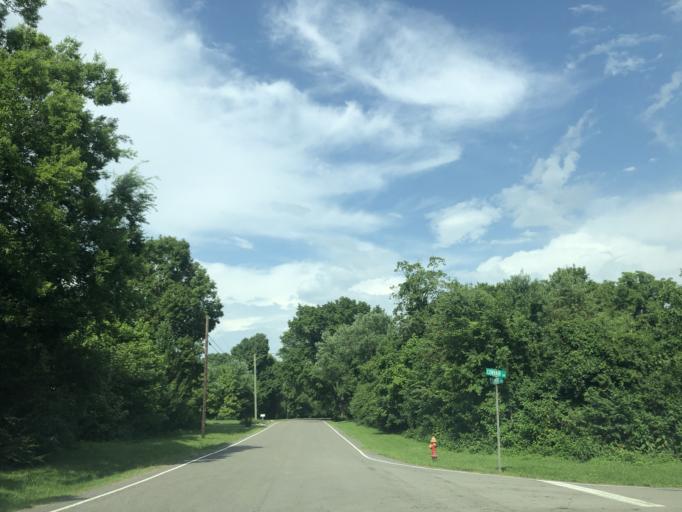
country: US
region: Tennessee
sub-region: Davidson County
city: Oak Hill
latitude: 36.1080
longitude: -86.6931
